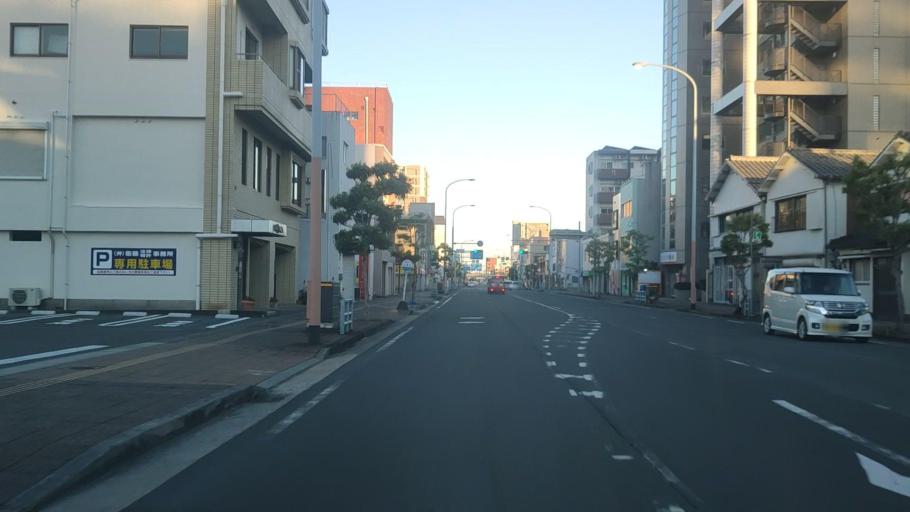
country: JP
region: Miyazaki
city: Miyazaki-shi
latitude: 31.9082
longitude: 131.4248
